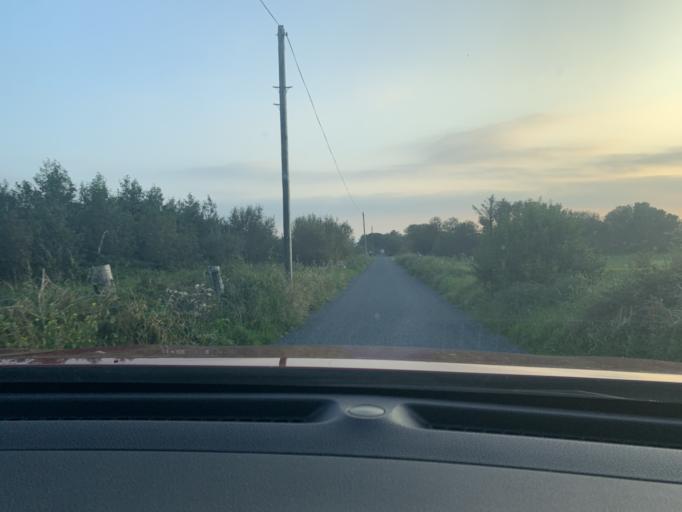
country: IE
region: Connaught
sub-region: County Leitrim
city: Kinlough
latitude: 54.4354
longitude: -8.4348
